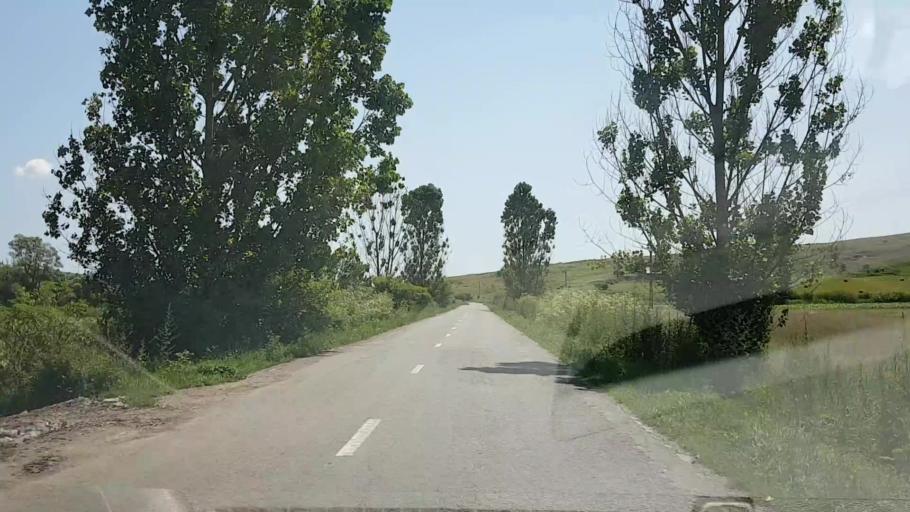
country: RO
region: Sibiu
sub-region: Comuna Merghindeal
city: Merghindeal
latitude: 45.9623
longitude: 24.7390
